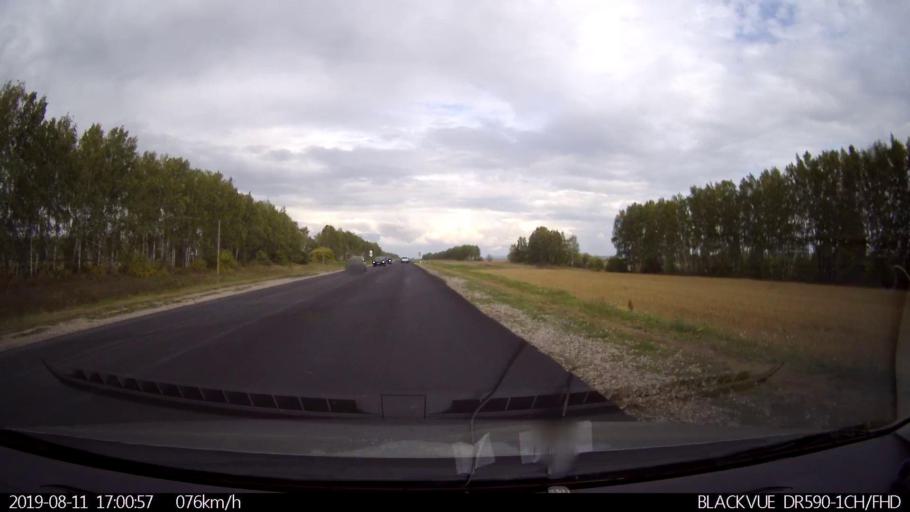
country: RU
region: Ulyanovsk
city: Mayna
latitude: 54.3093
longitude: 47.6884
